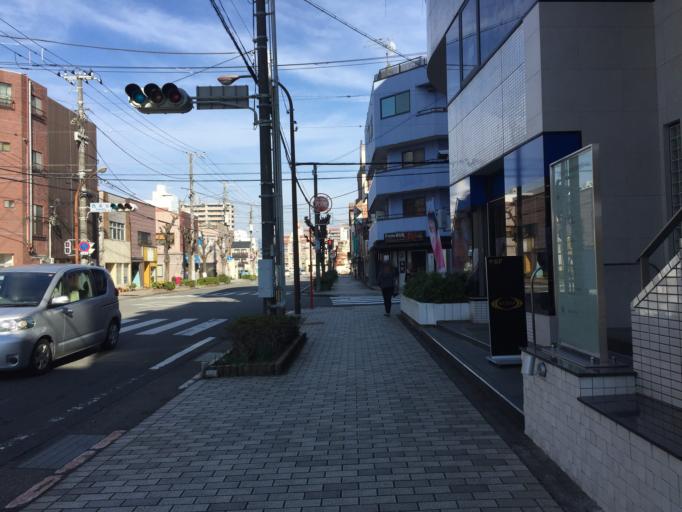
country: JP
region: Shizuoka
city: Numazu
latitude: 35.1005
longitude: 138.8558
